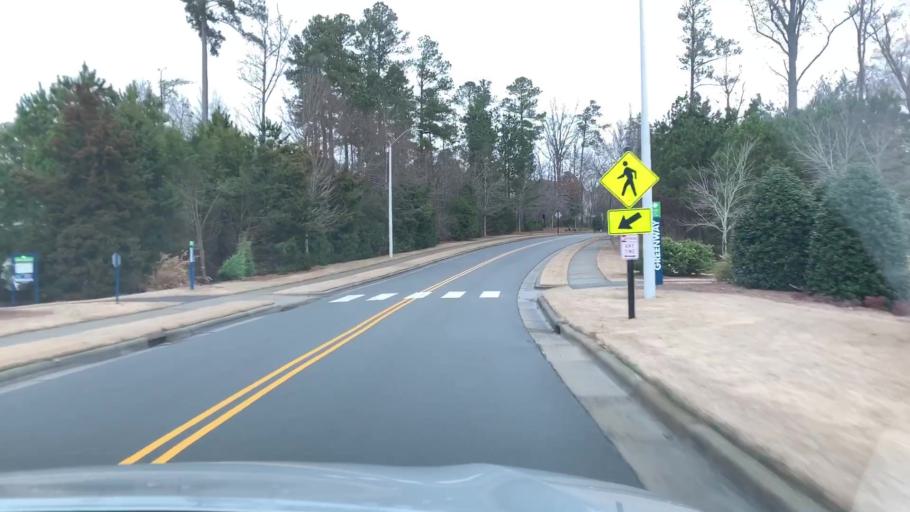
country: US
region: North Carolina
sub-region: Wake County
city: Green Level
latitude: 35.8171
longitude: -78.9056
